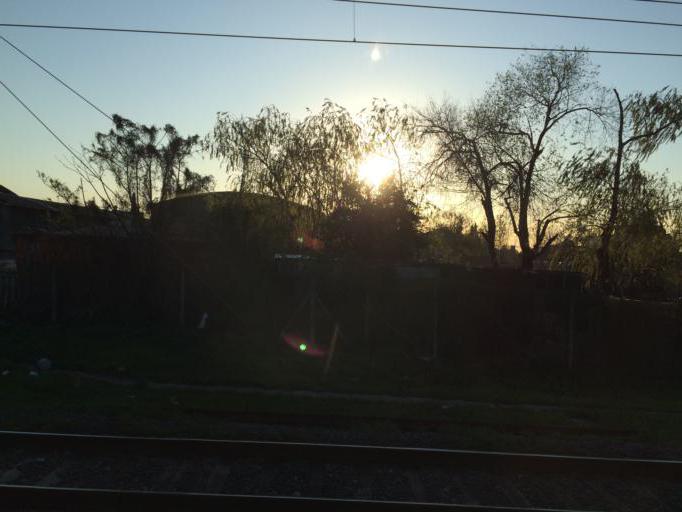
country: AR
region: Buenos Aires
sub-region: Partido de Lanus
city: Lanus
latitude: -34.7195
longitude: -58.3928
